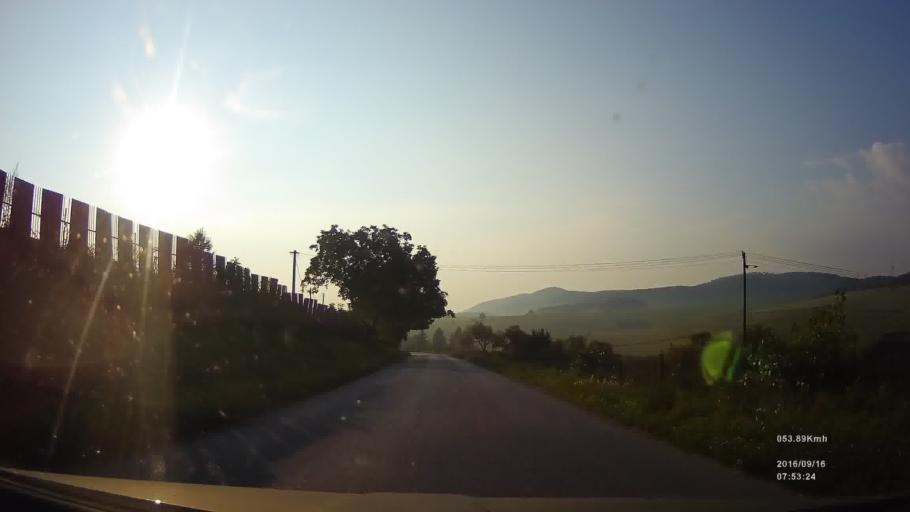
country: SK
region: Presovsky
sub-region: Okres Presov
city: Presov
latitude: 48.9188
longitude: 21.1079
